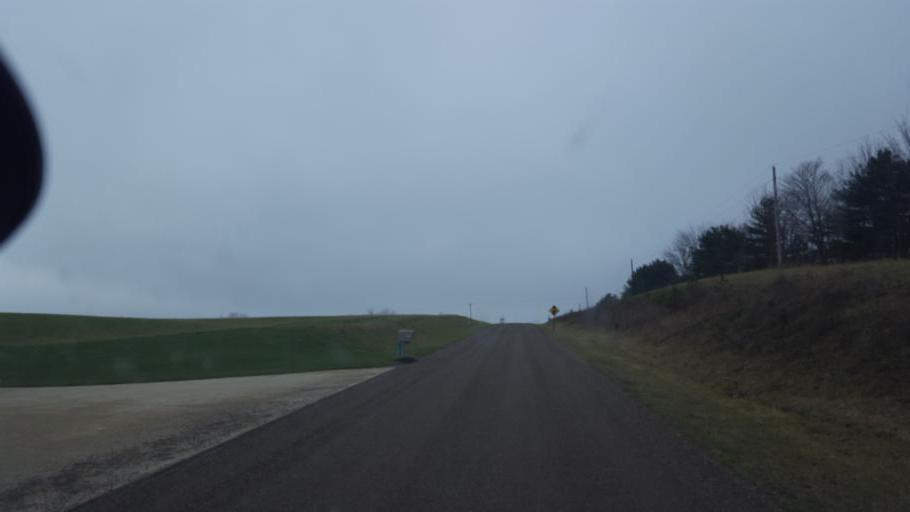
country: US
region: Ohio
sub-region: Richland County
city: Lexington
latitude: 40.5682
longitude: -82.6213
